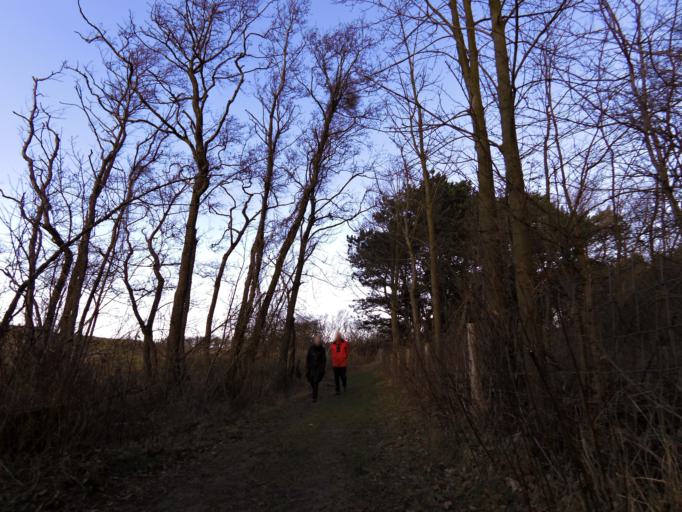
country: NL
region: South Holland
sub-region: Gemeente Goeree-Overflakkee
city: Goedereede
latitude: 51.8907
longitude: 4.0448
